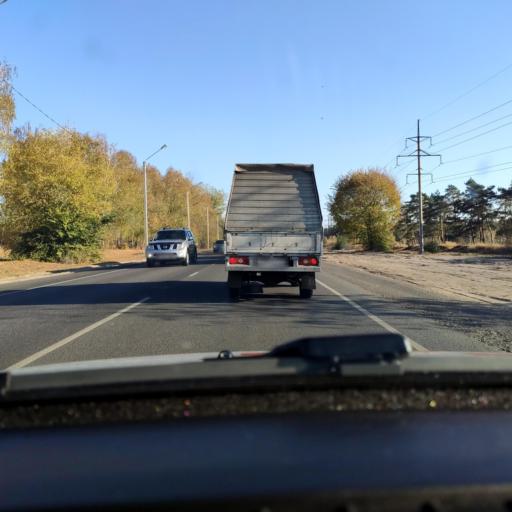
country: RU
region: Voronezj
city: Pridonskoy
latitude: 51.6980
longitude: 39.0827
